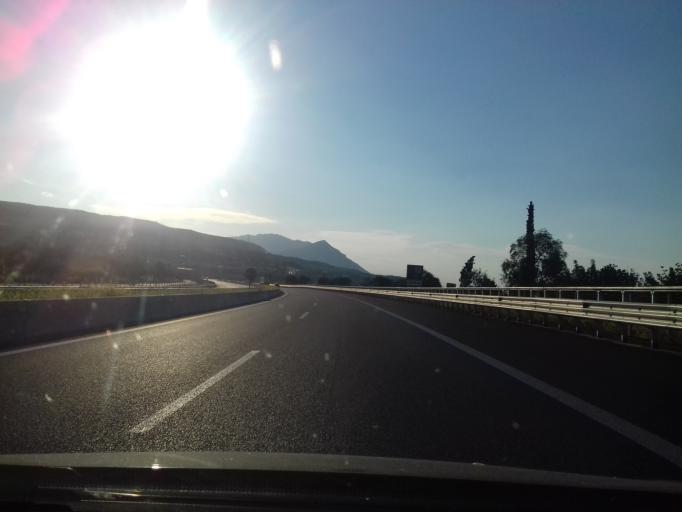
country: GR
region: Peloponnese
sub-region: Nomos Korinthias
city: Xylokastro
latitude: 38.0566
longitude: 22.6697
